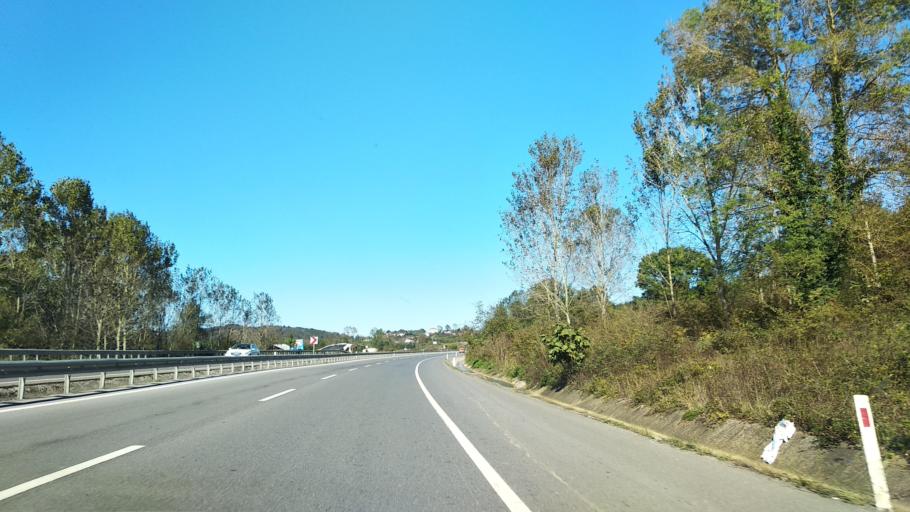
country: TR
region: Sakarya
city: Ortakoy
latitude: 41.0372
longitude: 30.6184
